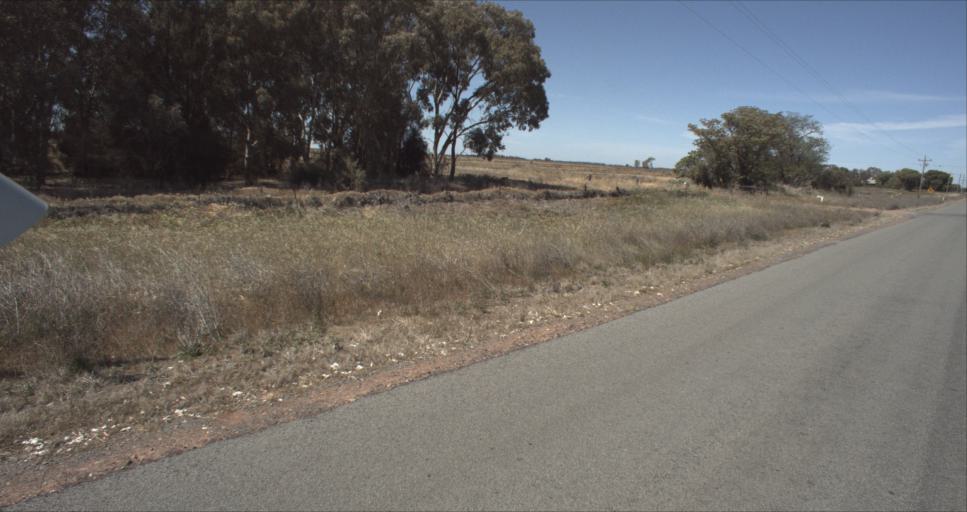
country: AU
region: New South Wales
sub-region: Leeton
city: Leeton
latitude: -34.4372
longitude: 146.2985
